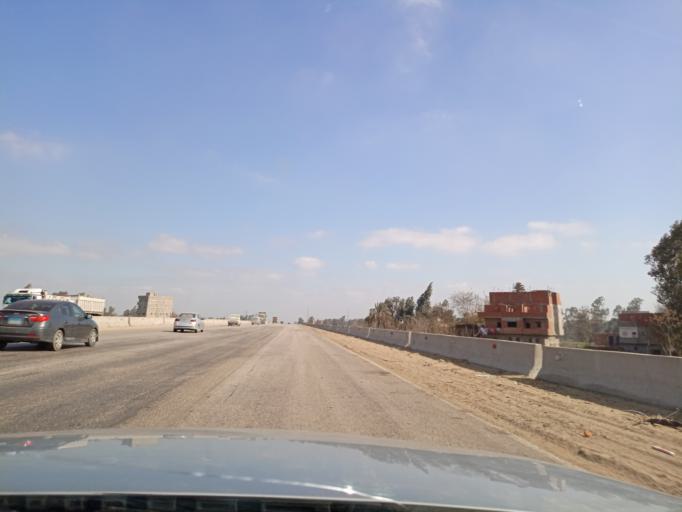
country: EG
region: Muhafazat al Minufiyah
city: Al Bajur
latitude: 30.4304
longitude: 31.0984
